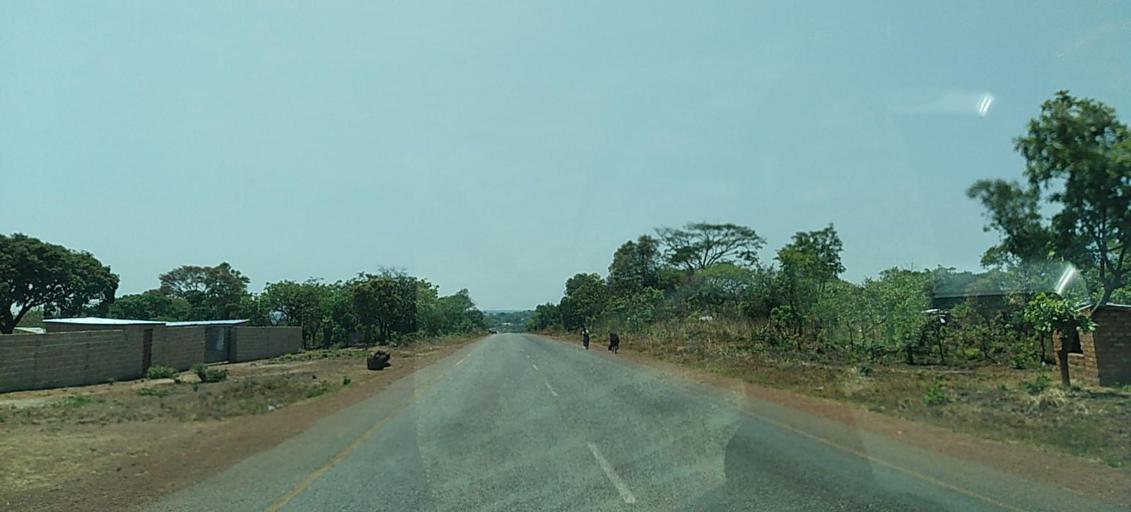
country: ZM
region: North-Western
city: Solwezi
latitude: -12.3943
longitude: 26.2247
